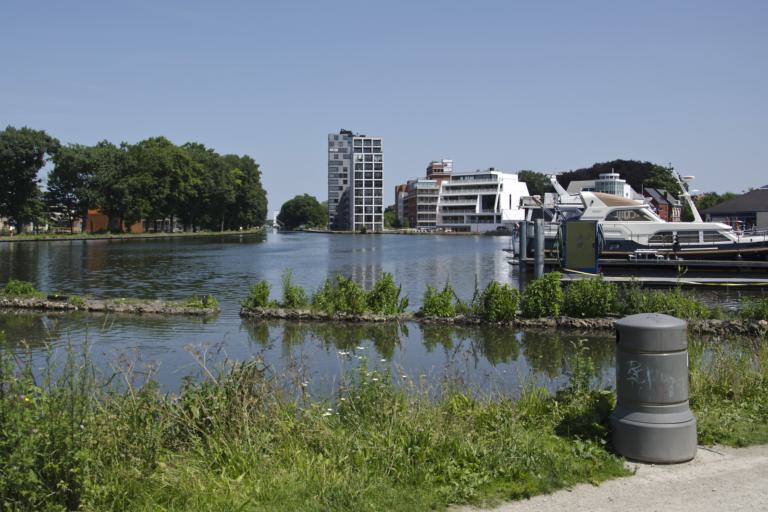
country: BE
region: Flanders
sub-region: Provincie Antwerpen
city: Turnhout
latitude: 51.3263
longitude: 4.9302
